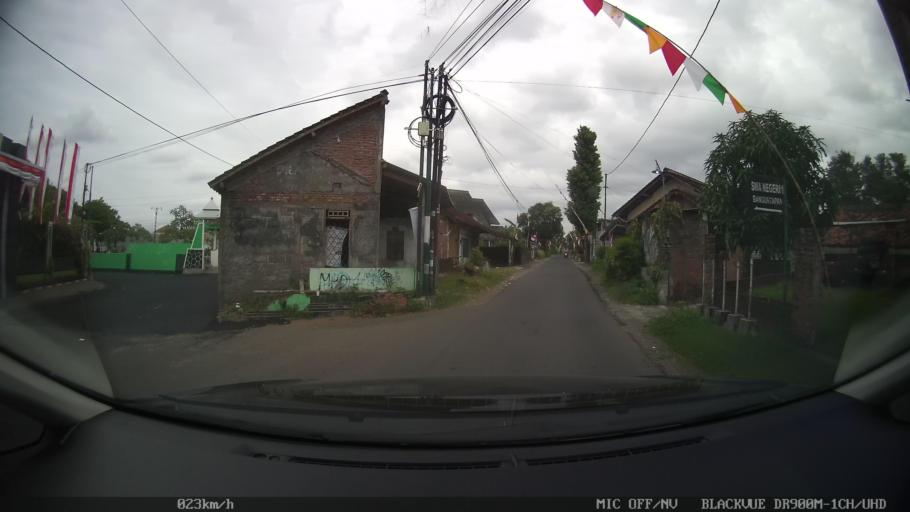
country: ID
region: Daerah Istimewa Yogyakarta
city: Depok
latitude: -7.8092
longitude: 110.4176
